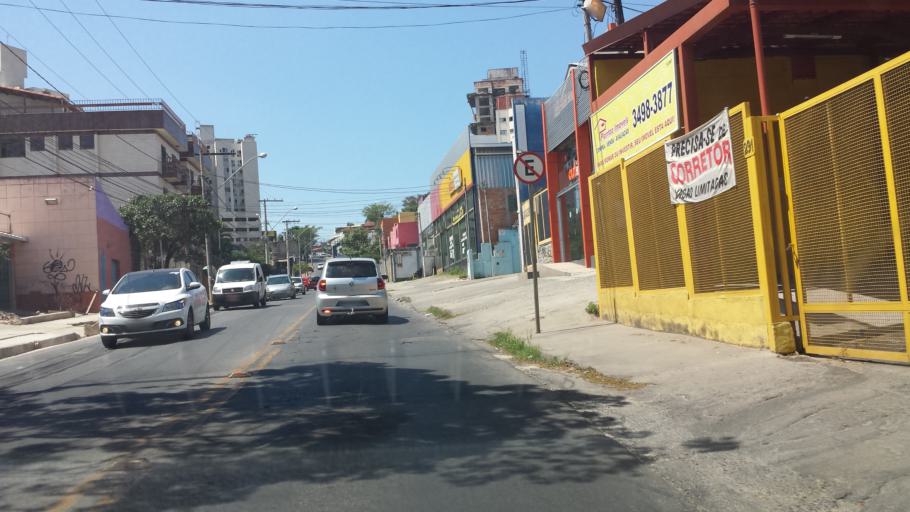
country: BR
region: Minas Gerais
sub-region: Belo Horizonte
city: Belo Horizonte
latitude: -19.8749
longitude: -43.9913
